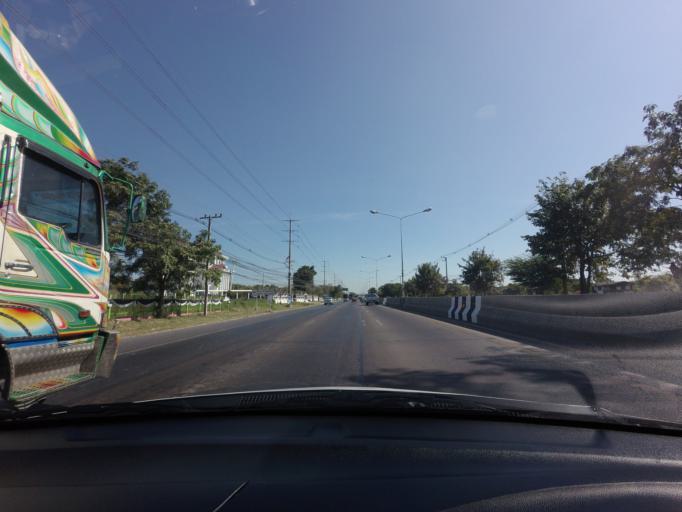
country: TH
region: Pathum Thani
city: Thanyaburi
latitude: 14.0156
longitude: 100.7236
